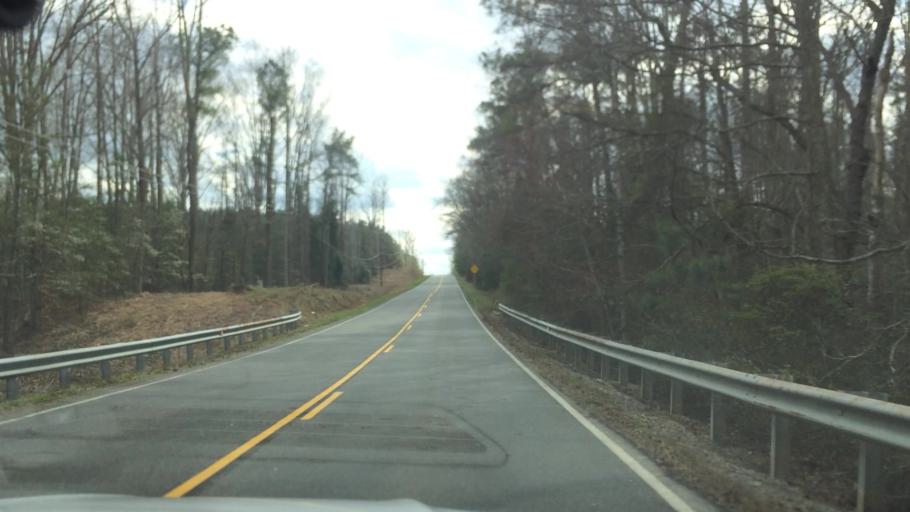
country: US
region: Virginia
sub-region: New Kent County
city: New Kent
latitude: 37.5074
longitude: -77.0171
